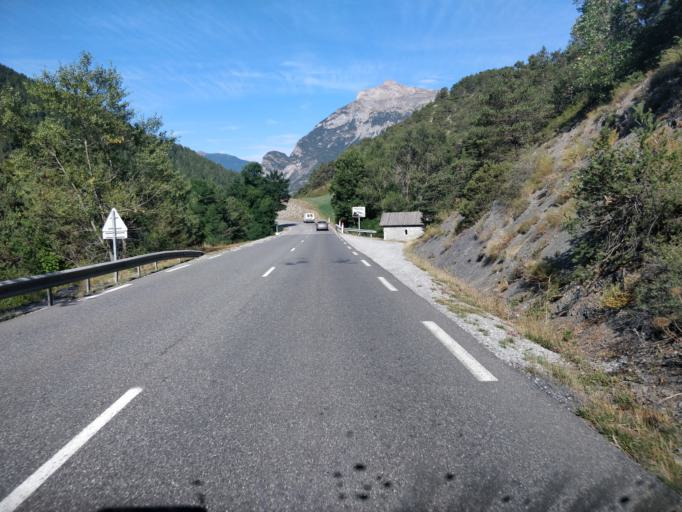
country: FR
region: Provence-Alpes-Cote d'Azur
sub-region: Departement des Alpes-de-Haute-Provence
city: Barcelonnette
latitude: 44.3935
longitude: 6.5545
